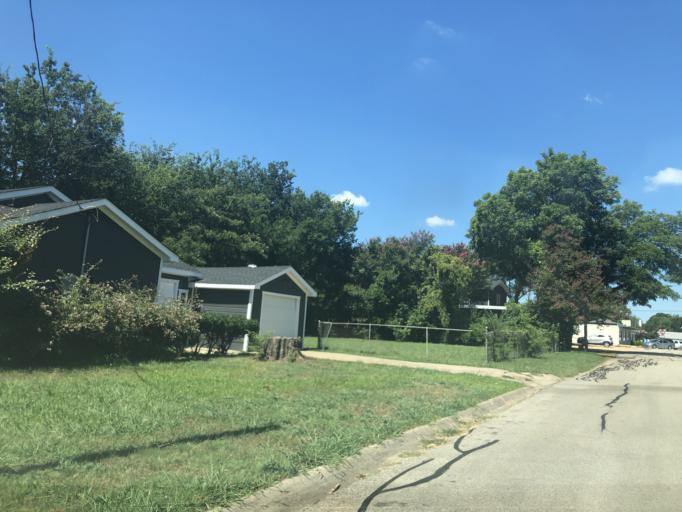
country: US
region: Texas
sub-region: Dallas County
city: Duncanville
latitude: 32.6538
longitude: -96.9065
